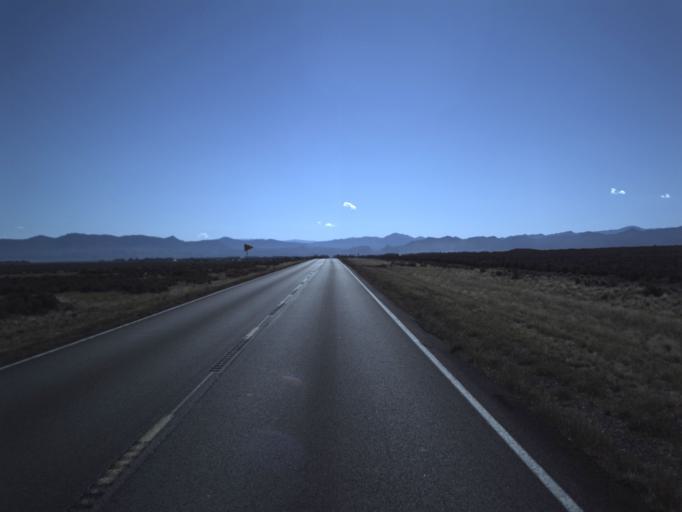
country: US
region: Utah
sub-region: Washington County
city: Enterprise
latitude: 37.7349
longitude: -113.7271
